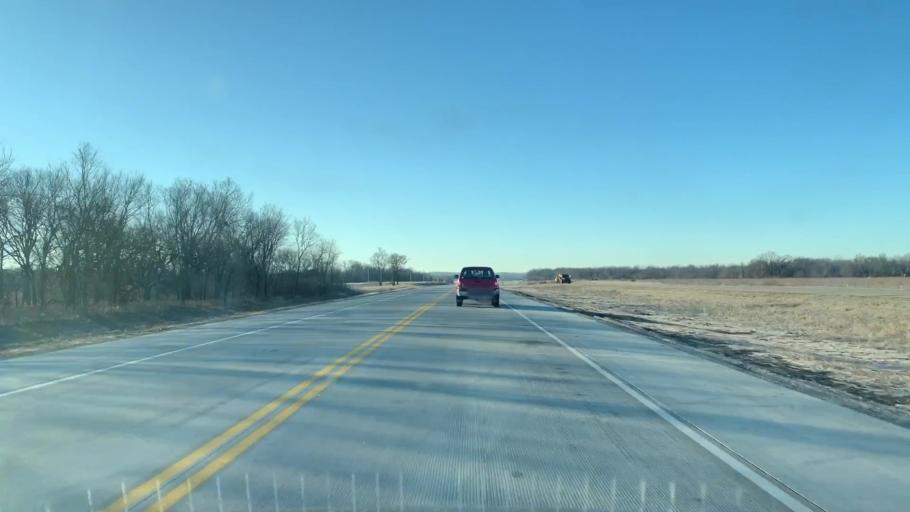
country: US
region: Kansas
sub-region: Bourbon County
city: Fort Scott
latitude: 37.7206
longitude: -94.7042
